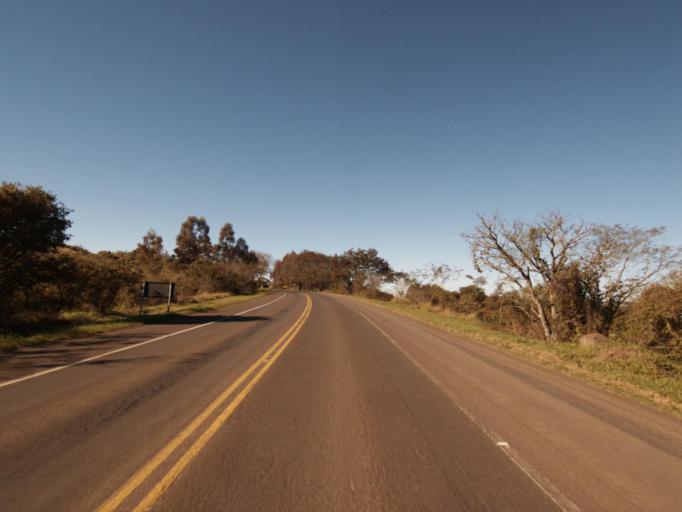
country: BR
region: Rio Grande do Sul
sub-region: Frederico Westphalen
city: Frederico Westphalen
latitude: -26.7997
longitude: -53.4490
